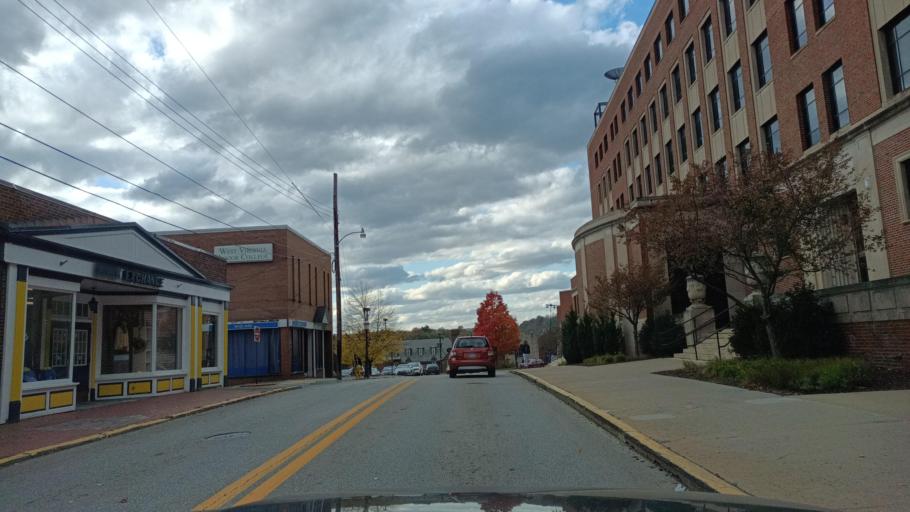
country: US
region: West Virginia
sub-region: Monongalia County
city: Morgantown
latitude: 39.6325
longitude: -79.9544
